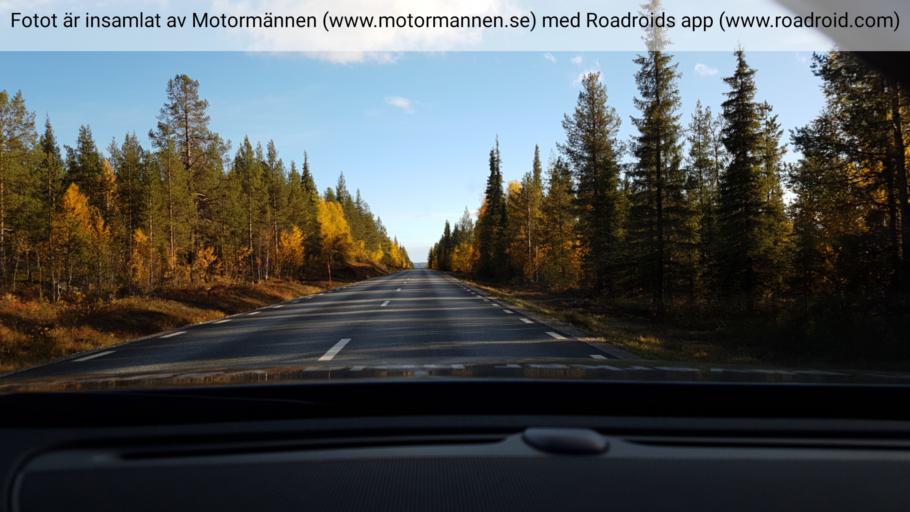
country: SE
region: Norrbotten
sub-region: Jokkmokks Kommun
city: Jokkmokk
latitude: 66.9024
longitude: 19.8270
